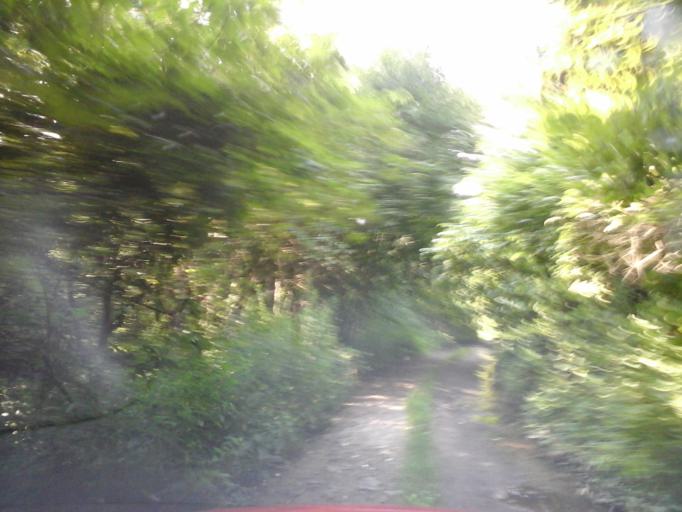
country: PL
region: West Pomeranian Voivodeship
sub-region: Powiat mysliborski
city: Barlinek
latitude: 53.0534
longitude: 15.1941
